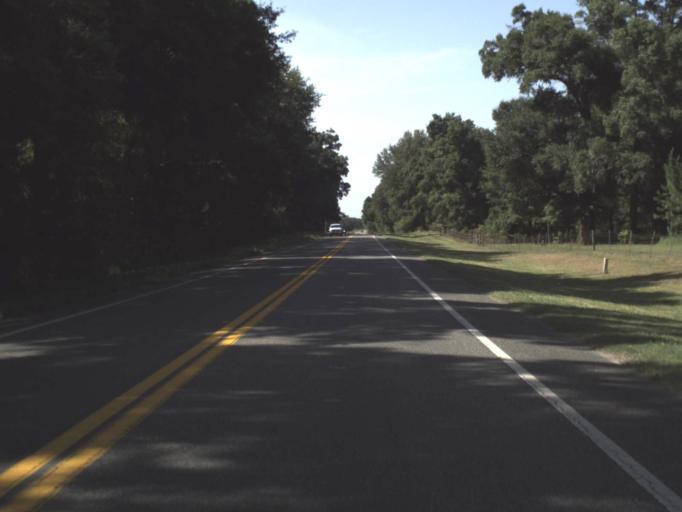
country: US
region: Florida
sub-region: Alachua County
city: High Springs
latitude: 29.9829
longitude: -82.7100
